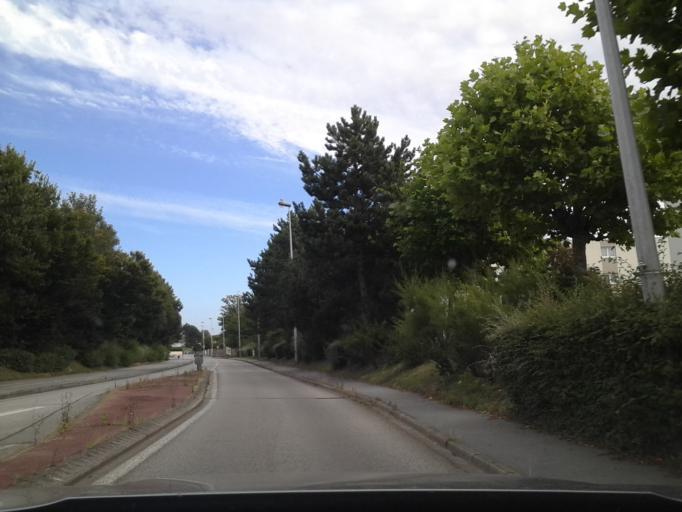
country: FR
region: Lower Normandy
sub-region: Departement de la Manche
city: Tourlaville
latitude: 49.6433
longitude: -1.5750
